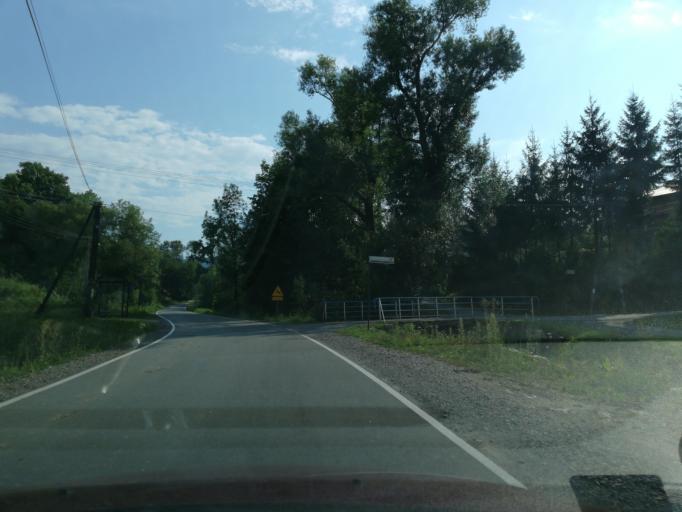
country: PL
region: Lesser Poland Voivodeship
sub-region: Powiat nowosadecki
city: Nawojowa
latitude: 49.5543
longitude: 20.7454
